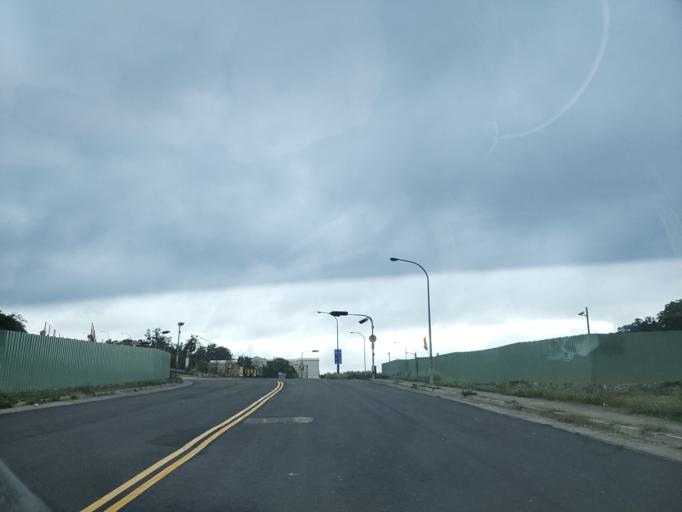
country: TW
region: Taiwan
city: Fengyuan
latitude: 24.3881
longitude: 120.7583
